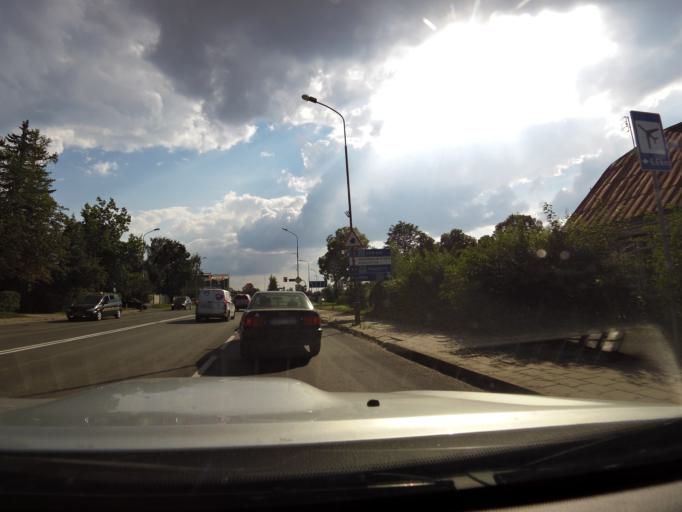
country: LT
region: Siauliu apskritis
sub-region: Siauliai
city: Siauliai
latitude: 55.9304
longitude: 23.2989
